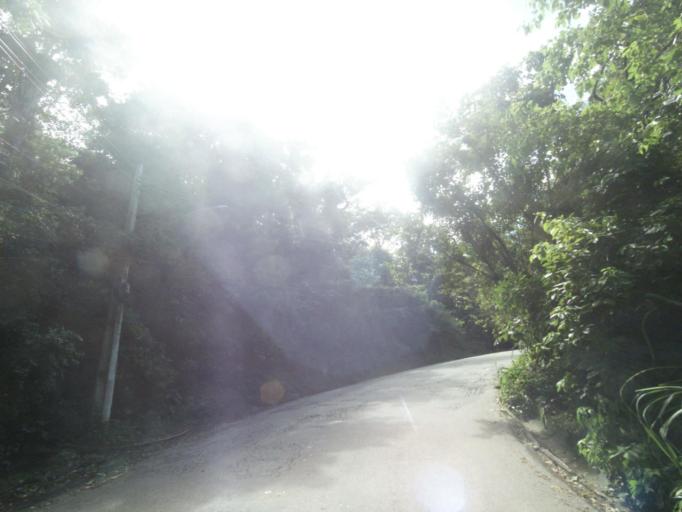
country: BR
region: Rio de Janeiro
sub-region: Niteroi
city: Niteroi
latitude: -22.9628
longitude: -43.0223
